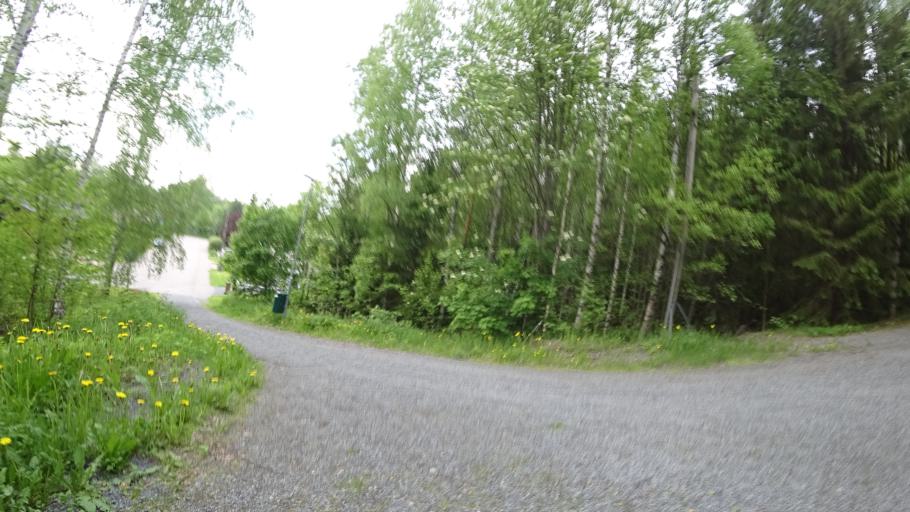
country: FI
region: Pirkanmaa
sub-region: Tampere
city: Yloejaervi
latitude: 61.5218
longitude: 23.6082
